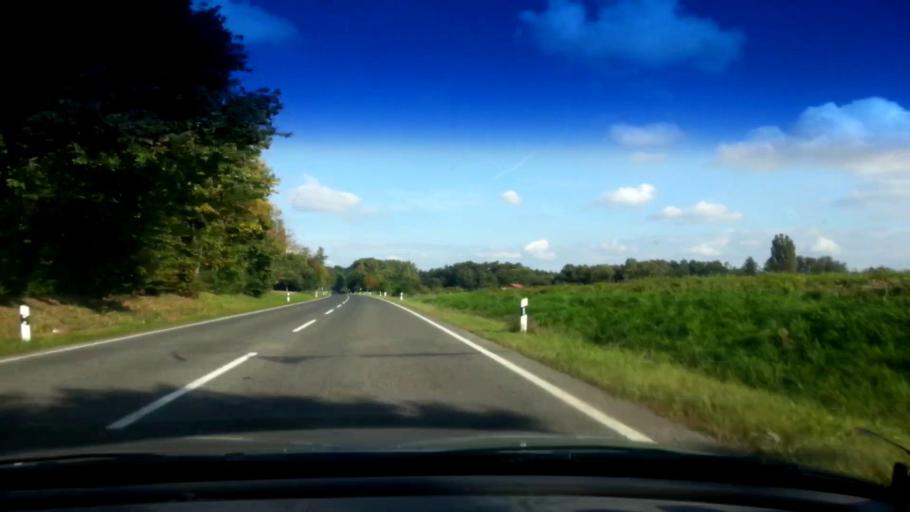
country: DE
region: Bavaria
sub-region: Upper Franconia
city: Bischberg
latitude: 49.9312
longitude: 10.8401
